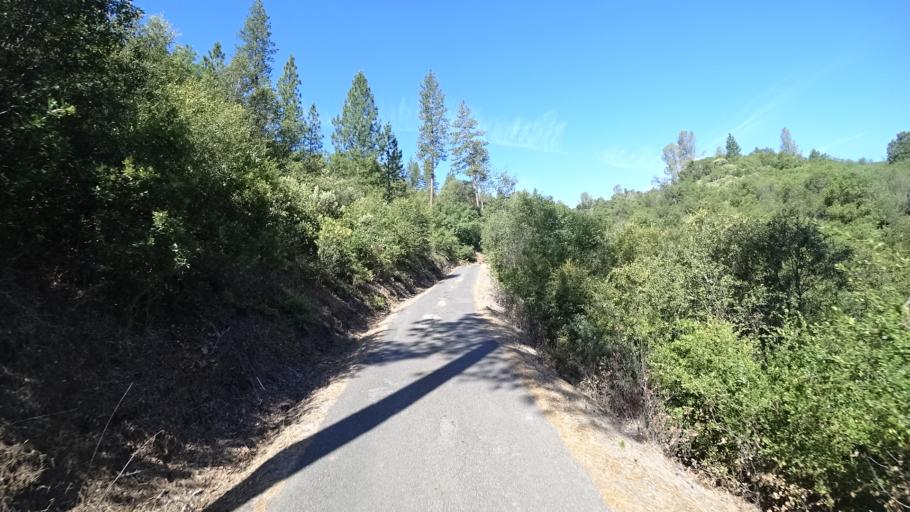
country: US
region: California
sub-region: Calaveras County
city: Mountain Ranch
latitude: 38.1632
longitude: -120.5438
